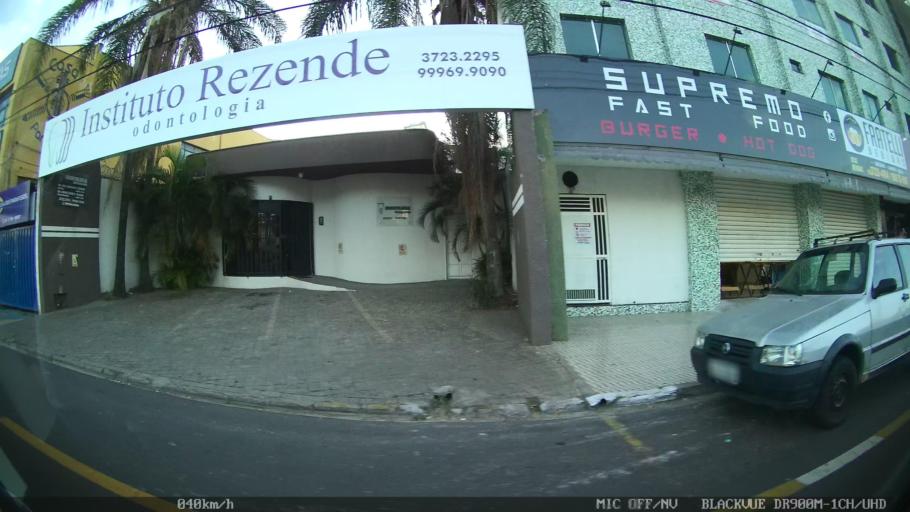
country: BR
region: Sao Paulo
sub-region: Franca
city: Franca
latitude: -20.5282
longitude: -47.4029
